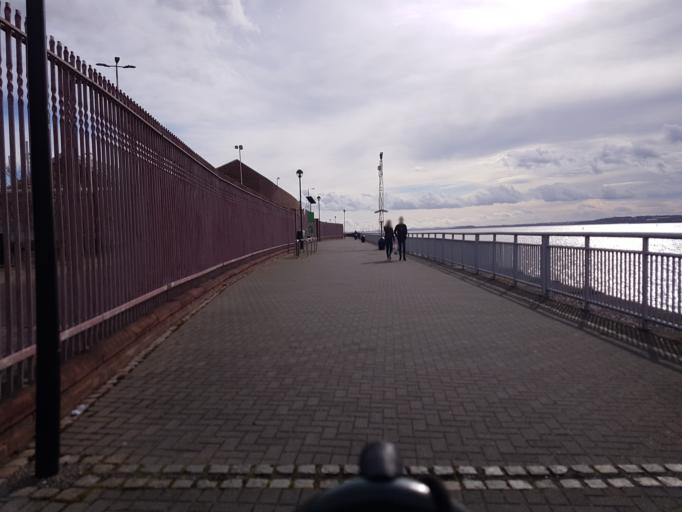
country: GB
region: England
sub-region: Metropolitan Borough of Wirral
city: New Ferry
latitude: 53.3820
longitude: -2.9793
